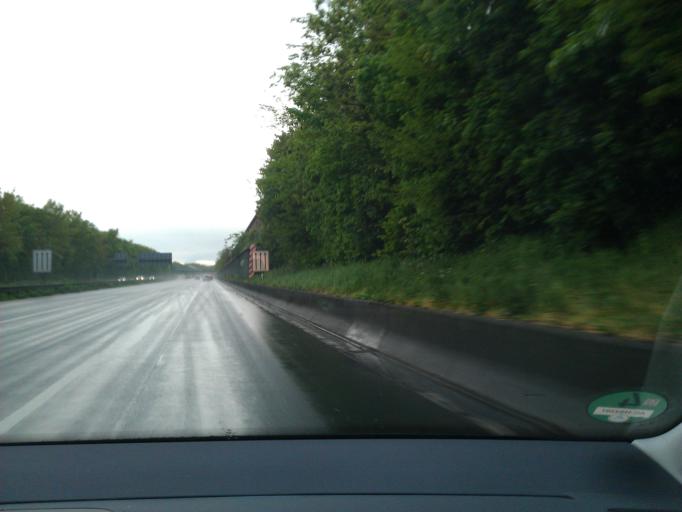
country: DE
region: North Rhine-Westphalia
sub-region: Regierungsbezirk Koln
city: Bonn
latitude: 50.7480
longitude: 7.0692
